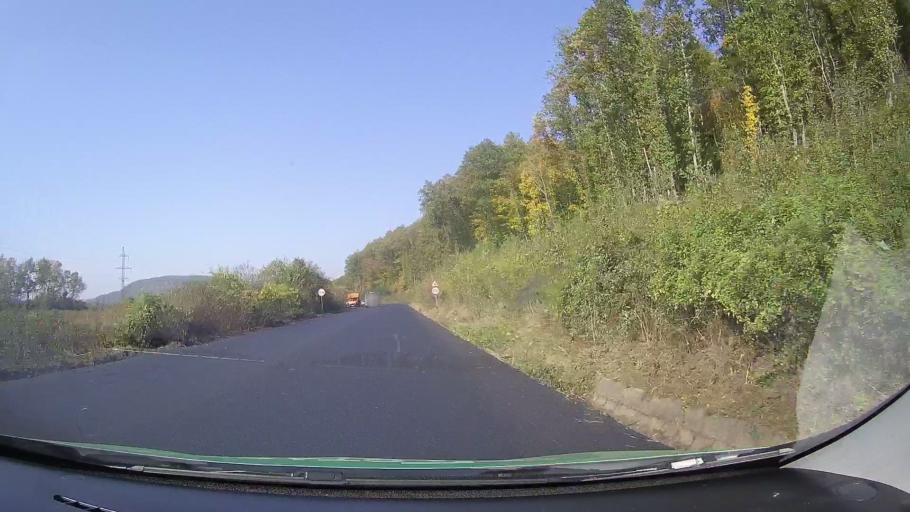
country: RO
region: Hunedoara
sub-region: Comuna Zam
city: Zam
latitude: 46.0159
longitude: 22.4212
